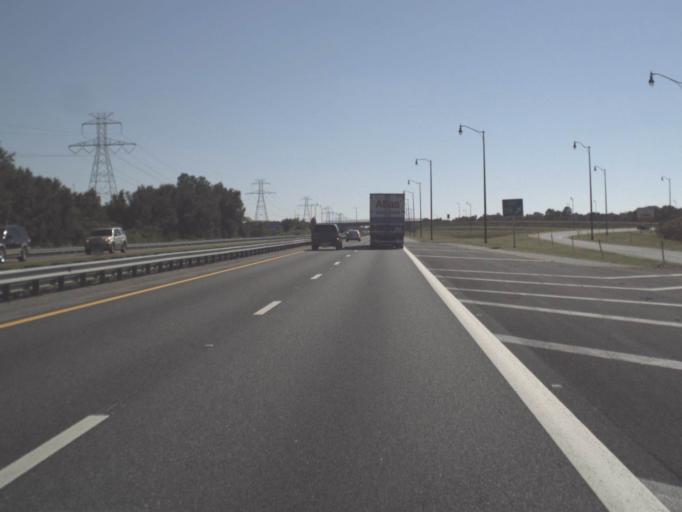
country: US
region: Florida
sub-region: Lake County
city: Hawthorne
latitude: 28.7600
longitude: -81.9438
